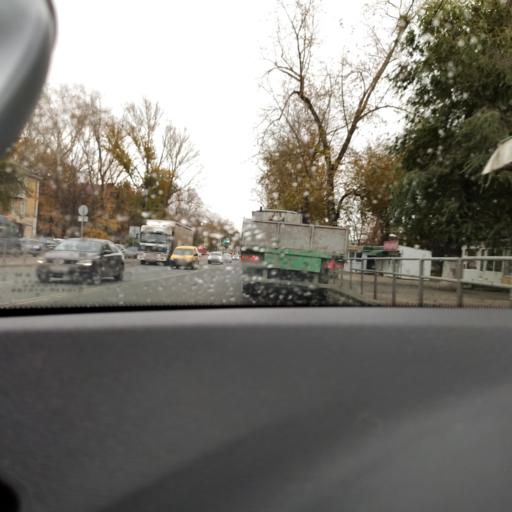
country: RU
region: Samara
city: Smyshlyayevka
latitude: 53.2154
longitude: 50.2922
